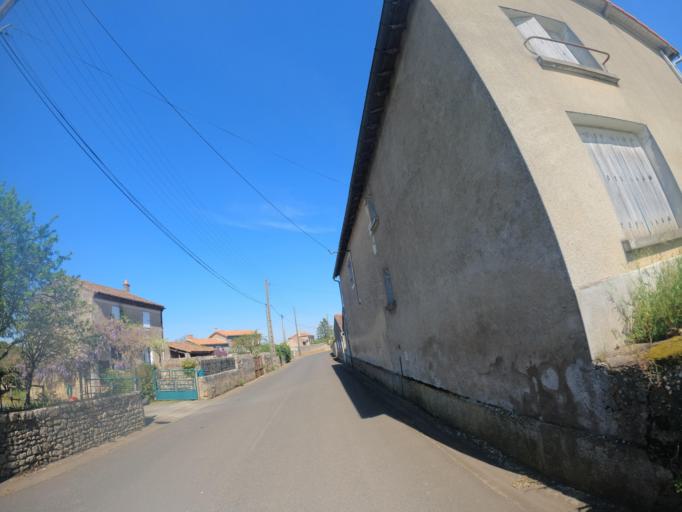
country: FR
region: Poitou-Charentes
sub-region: Departement des Deux-Sevres
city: Airvault
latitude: 46.8829
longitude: -0.1363
